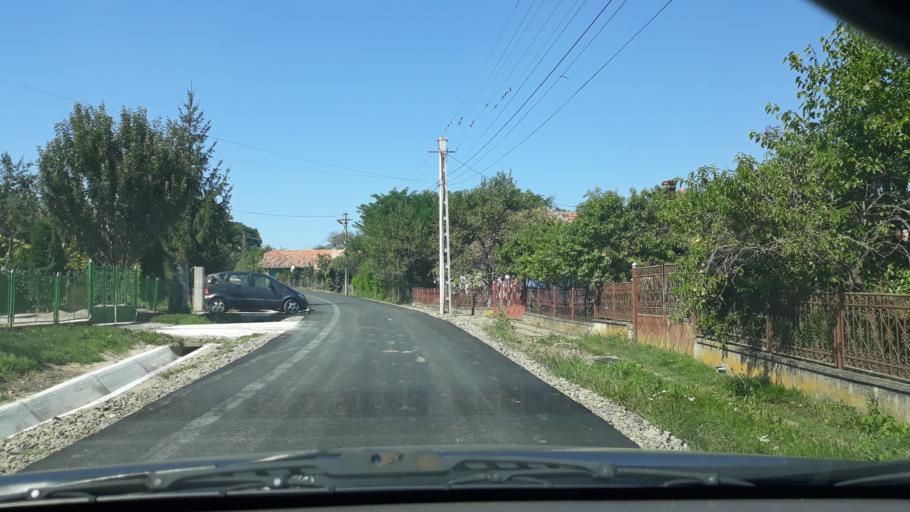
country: RO
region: Salaj
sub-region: Comuna Dobrin
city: Dobrin
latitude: 47.2931
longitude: 23.0903
